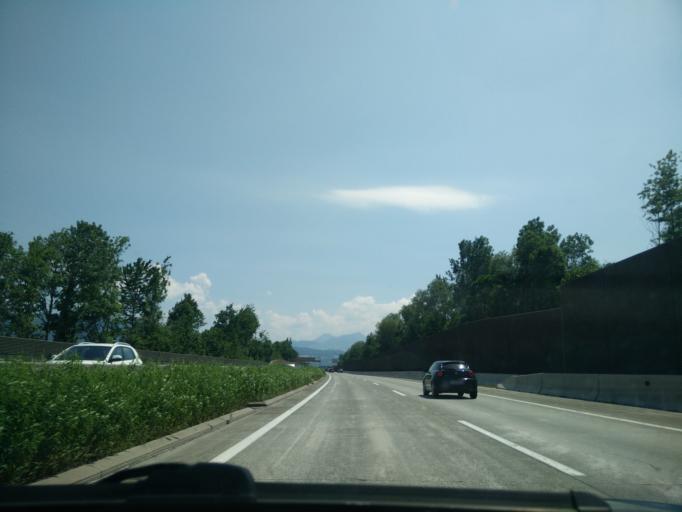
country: AT
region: Salzburg
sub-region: Politischer Bezirk Salzburg-Umgebung
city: Grodig
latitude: 47.7501
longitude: 13.0178
